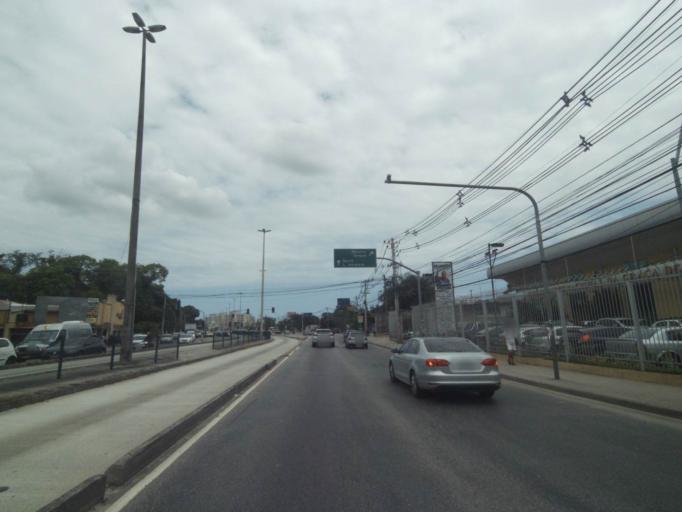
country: BR
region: Rio de Janeiro
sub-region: Sao Joao De Meriti
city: Sao Joao de Meriti
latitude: -22.9320
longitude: -43.3732
